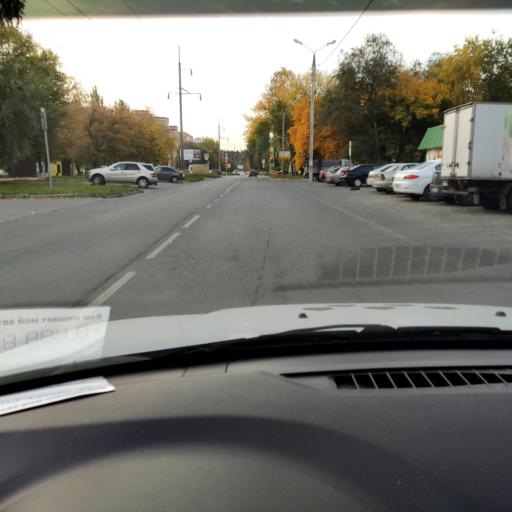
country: RU
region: Samara
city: Tol'yatti
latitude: 53.5123
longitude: 49.4424
